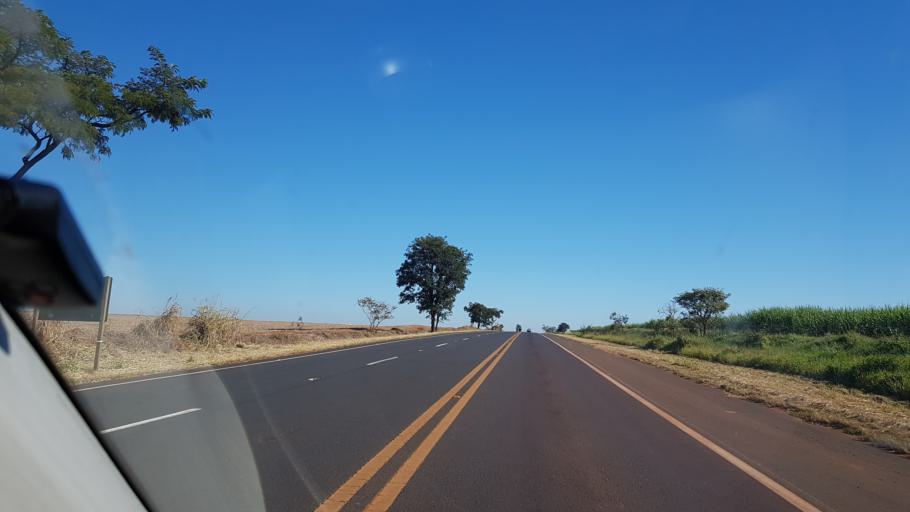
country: BR
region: Sao Paulo
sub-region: Assis
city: Assis
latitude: -22.5763
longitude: -50.5121
